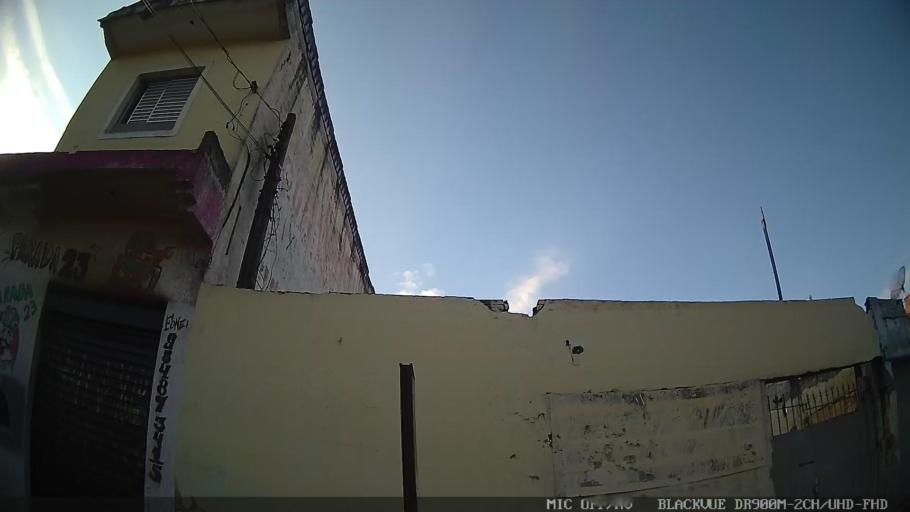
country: BR
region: Sao Paulo
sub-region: Ferraz De Vasconcelos
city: Ferraz de Vasconcelos
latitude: -23.5449
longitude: -46.4079
